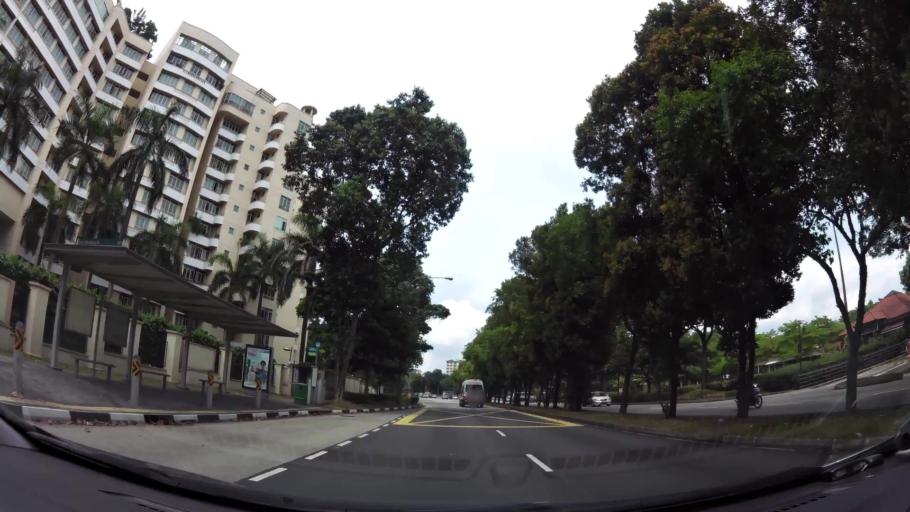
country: MY
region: Johor
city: Johor Bahru
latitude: 1.3877
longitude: 103.7460
